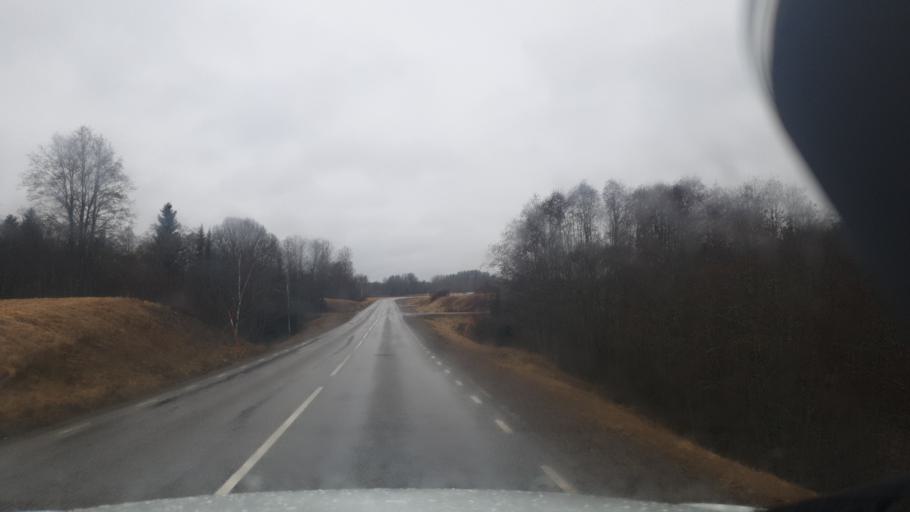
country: SE
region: Vaermland
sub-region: Arjangs Kommun
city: Arjaeng
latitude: 59.5637
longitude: 12.1218
